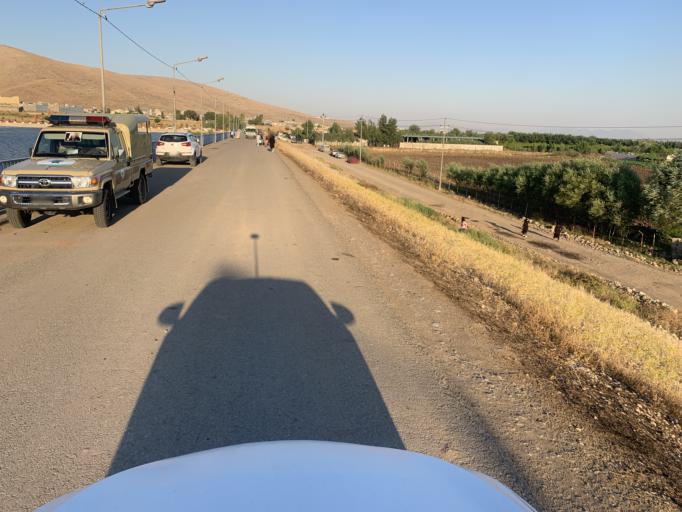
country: IQ
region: As Sulaymaniyah
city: Raniye
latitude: 36.2723
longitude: 44.7523
